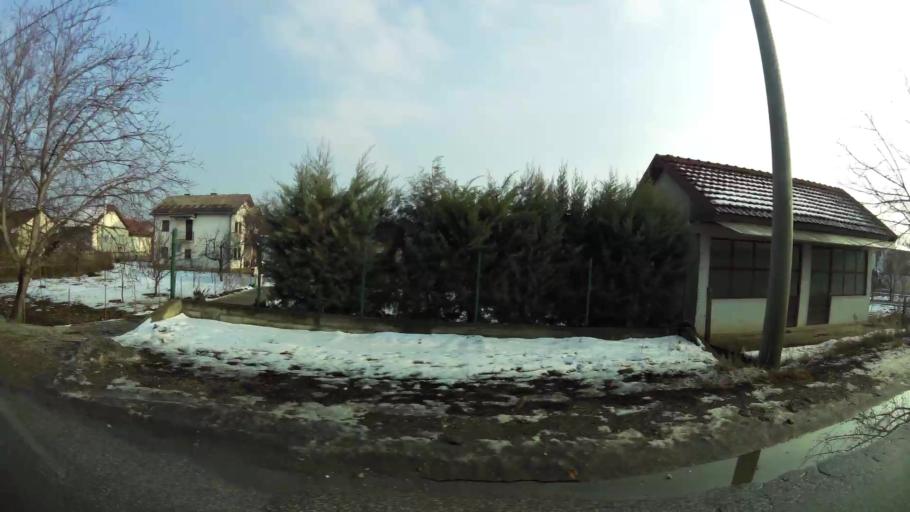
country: MK
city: Miladinovci
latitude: 41.9774
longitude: 21.6442
